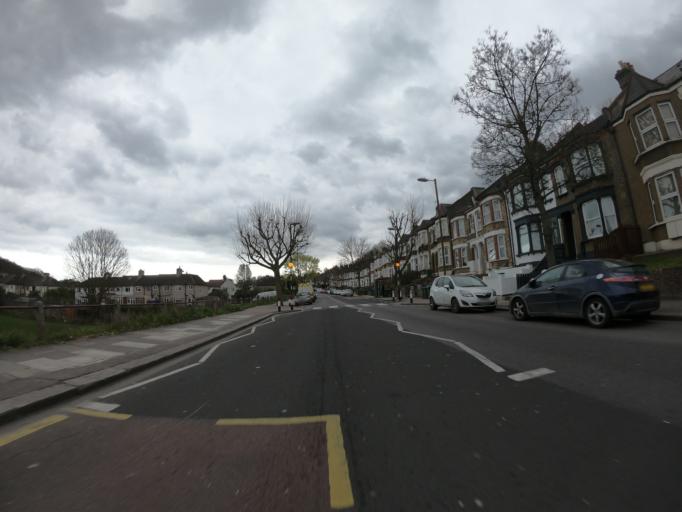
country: GB
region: England
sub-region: Greater London
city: Abbey Wood
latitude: 51.4821
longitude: 0.1018
